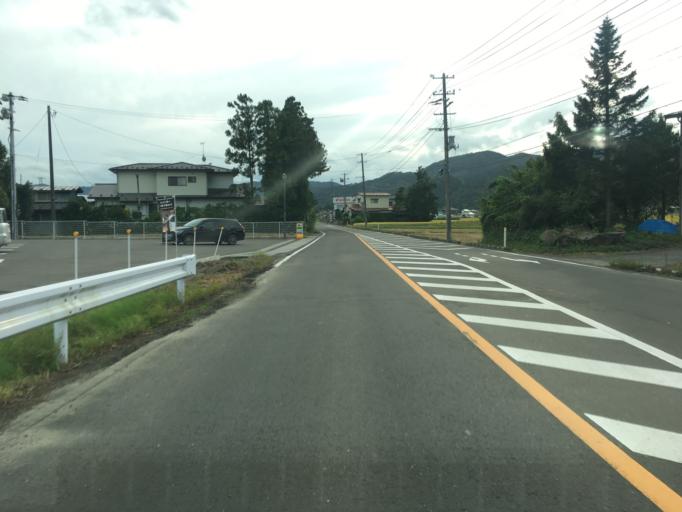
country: JP
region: Miyagi
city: Marumori
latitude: 37.9284
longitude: 140.7731
